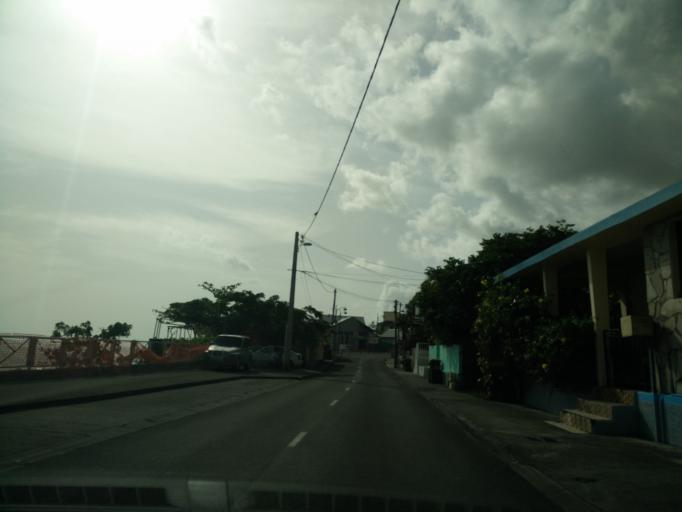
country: MQ
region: Martinique
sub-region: Martinique
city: Saint-Pierre
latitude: 14.7997
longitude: -61.2236
